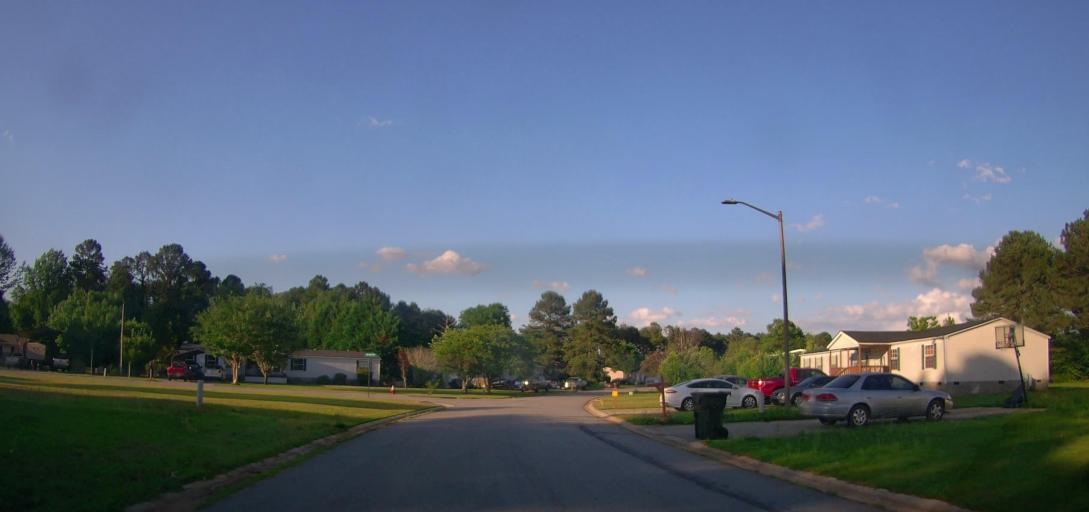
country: US
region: Georgia
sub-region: Houston County
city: Centerville
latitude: 32.6422
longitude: -83.7238
